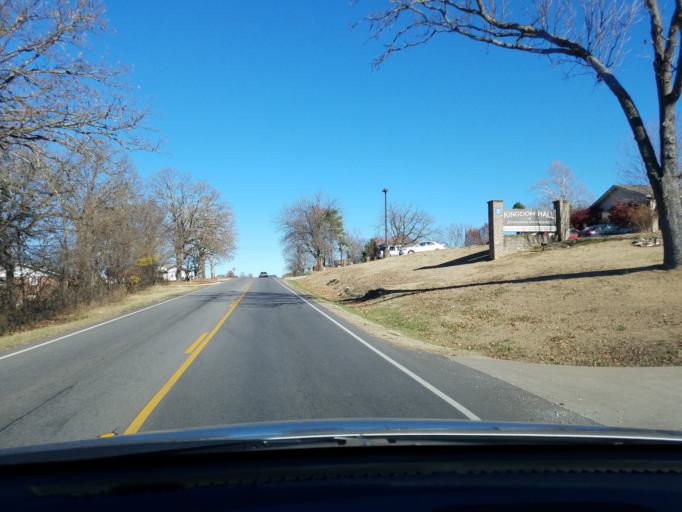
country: US
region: Arkansas
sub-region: Carroll County
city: Berryville
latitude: 36.3819
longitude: -93.5673
